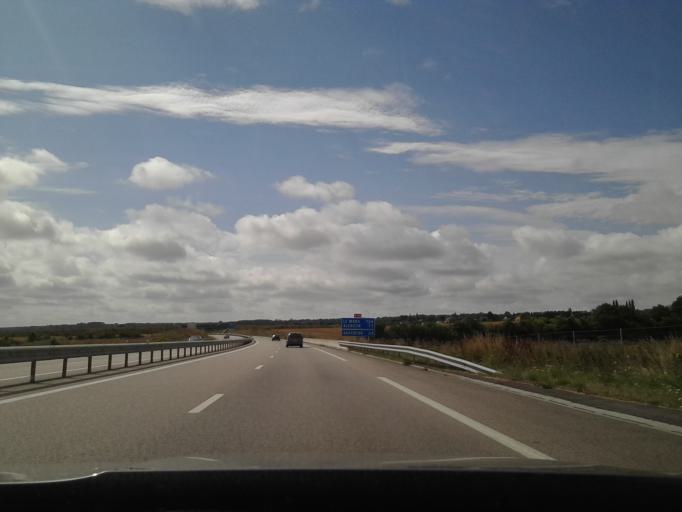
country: FR
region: Lower Normandy
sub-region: Departement du Calvados
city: Falaise
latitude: 48.8776
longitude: -0.2183
